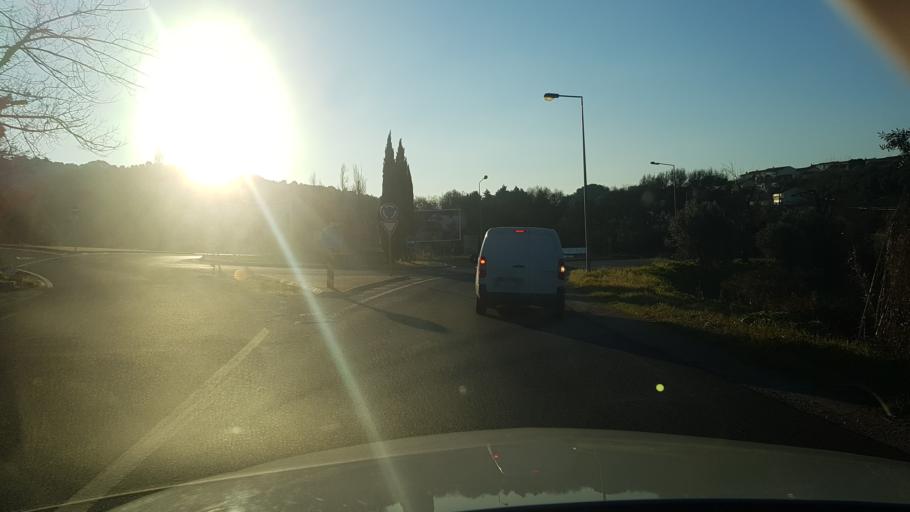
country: PT
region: Santarem
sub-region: Torres Novas
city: Torres Novas
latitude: 39.4889
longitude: -8.5380
